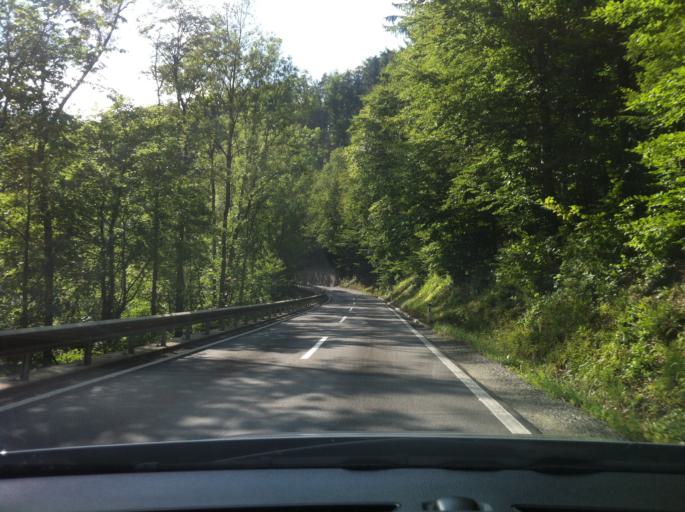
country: AT
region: Styria
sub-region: Politischer Bezirk Hartberg-Fuerstenfeld
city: Stubenberg
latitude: 47.2430
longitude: 15.7785
